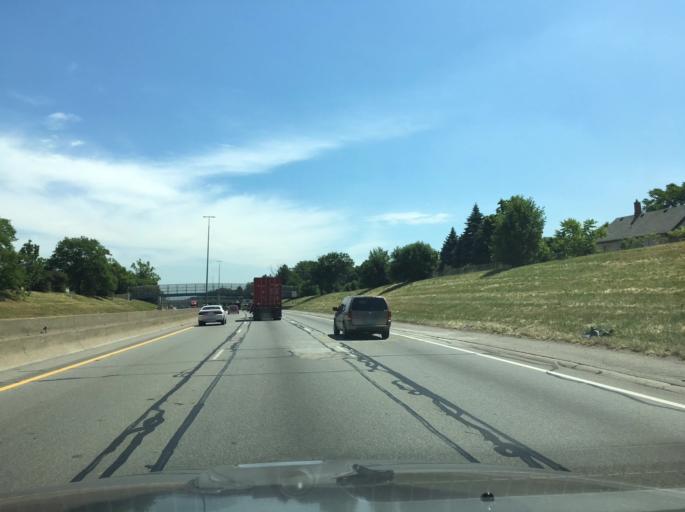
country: US
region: Michigan
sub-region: Wayne County
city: Dearborn
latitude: 42.3323
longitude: -83.1383
